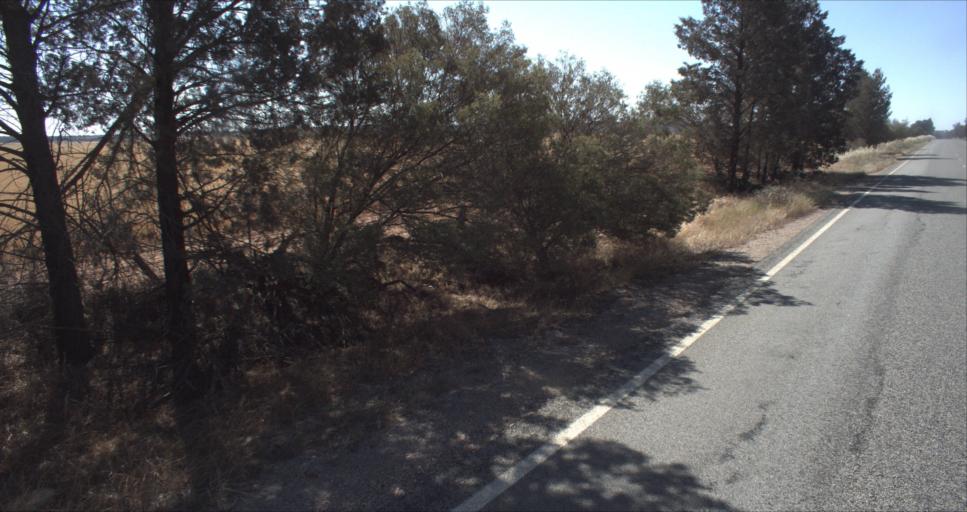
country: AU
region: New South Wales
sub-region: Leeton
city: Leeton
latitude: -34.4666
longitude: 146.4367
